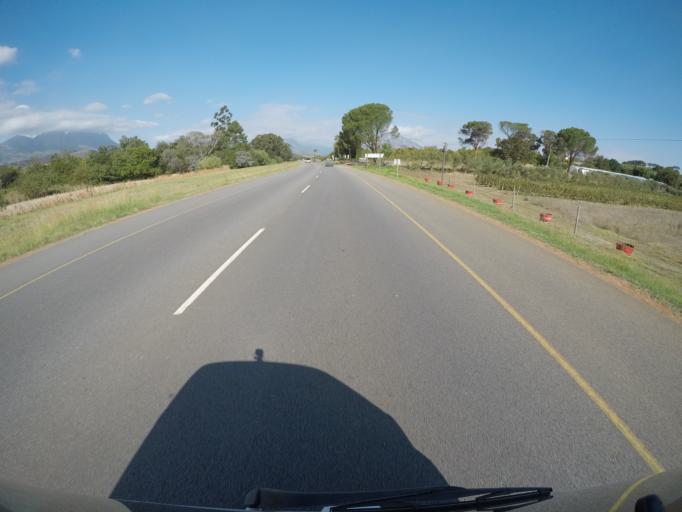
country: ZA
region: Western Cape
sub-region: Cape Winelands District Municipality
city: Stellenbosch
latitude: -33.8907
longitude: 18.8260
